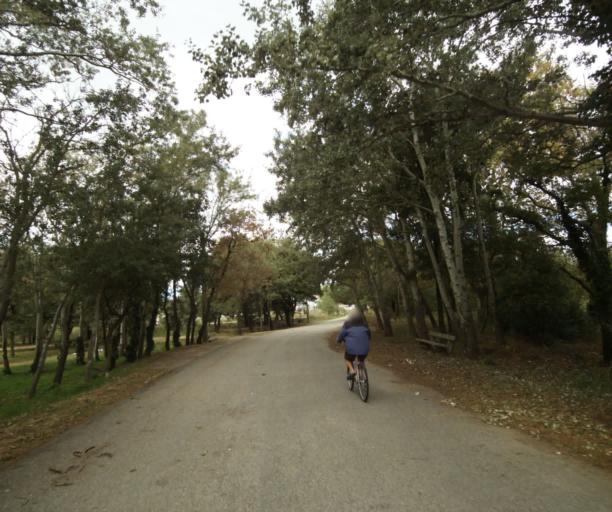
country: FR
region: Languedoc-Roussillon
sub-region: Departement des Pyrenees-Orientales
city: Argelers
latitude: 42.5394
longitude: 3.0517
